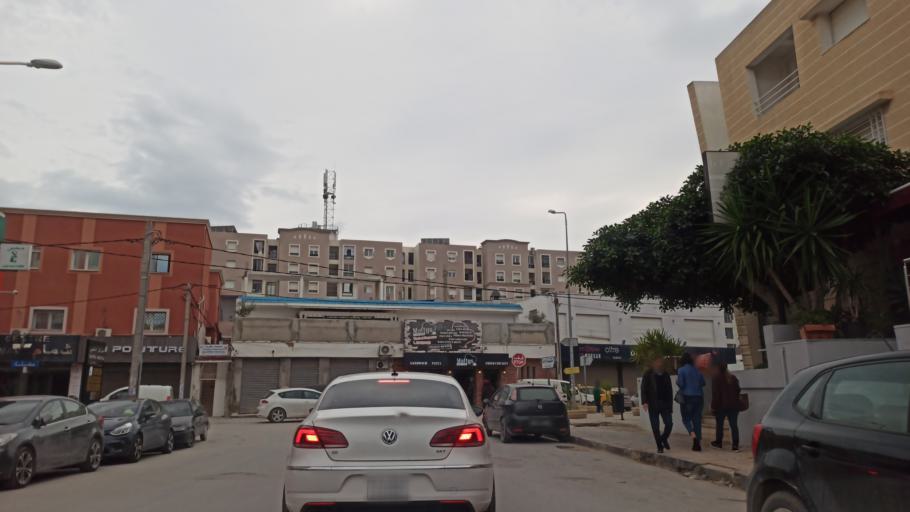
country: TN
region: Tunis
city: La Goulette
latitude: 36.8579
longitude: 10.2664
